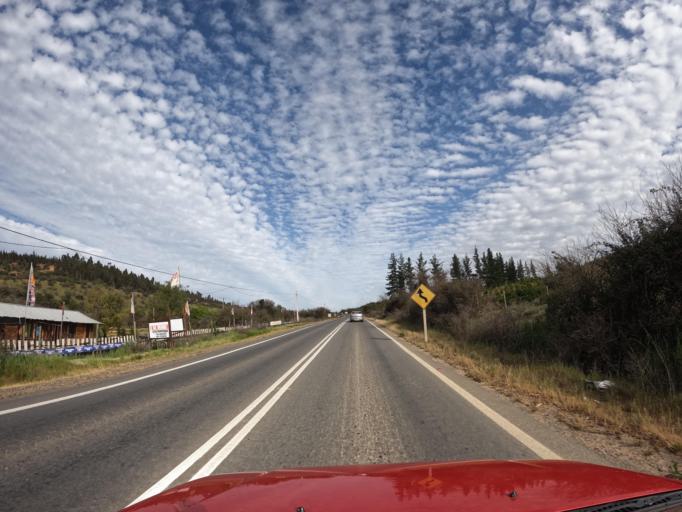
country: CL
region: O'Higgins
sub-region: Provincia de Colchagua
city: Santa Cruz
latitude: -34.3109
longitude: -71.7758
